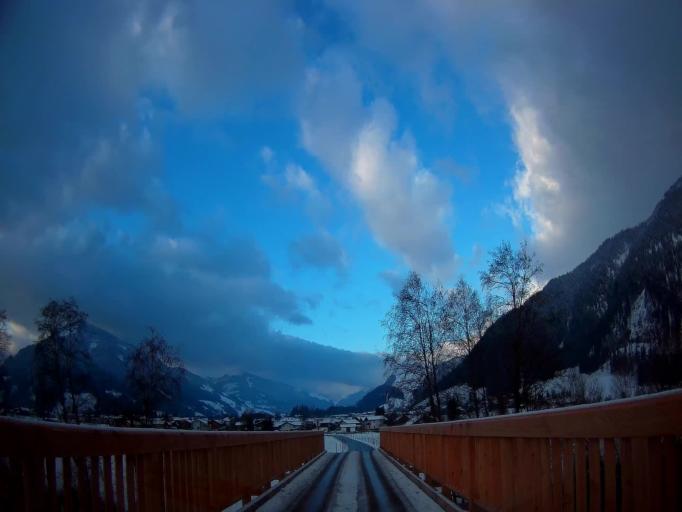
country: AT
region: Salzburg
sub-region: Politischer Bezirk Zell am See
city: Saalfelden am Steinernen Meer
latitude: 47.4526
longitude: 12.8236
